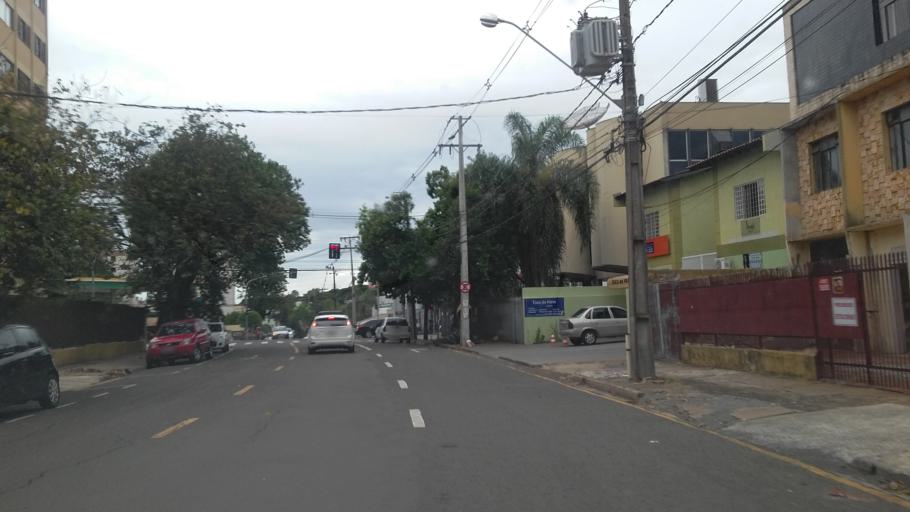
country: BR
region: Parana
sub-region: Londrina
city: Londrina
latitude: -23.3036
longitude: -51.1796
